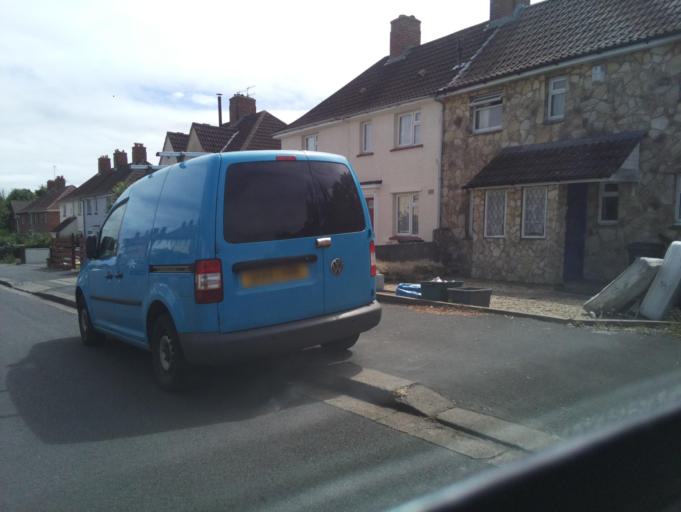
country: GB
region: England
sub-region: Bristol
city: Bristol
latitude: 51.4226
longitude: -2.5985
